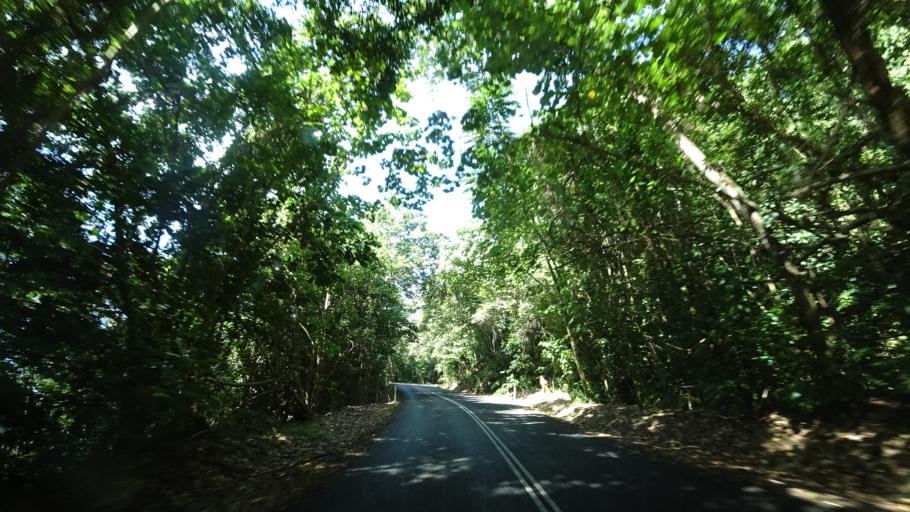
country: AU
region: Queensland
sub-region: Cairns
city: Port Douglas
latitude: -16.1191
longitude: 145.4573
